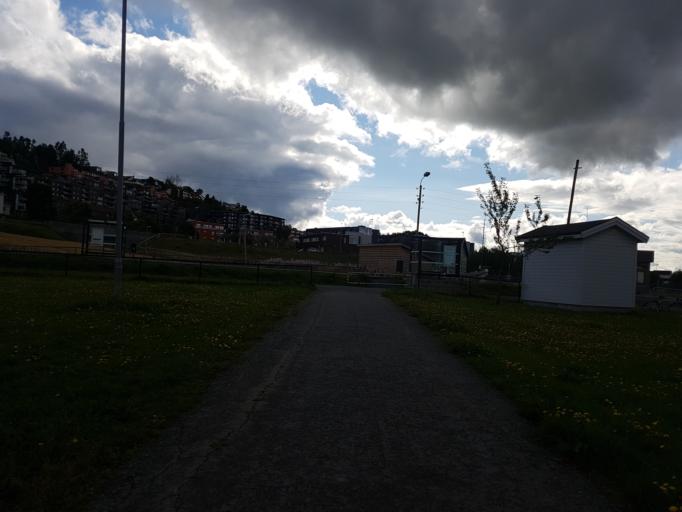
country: NO
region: Sor-Trondelag
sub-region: Trondheim
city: Trondheim
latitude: 63.4114
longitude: 10.4549
